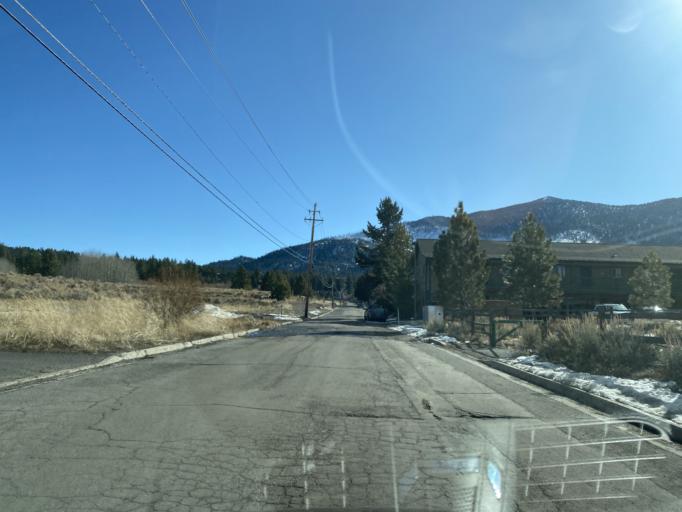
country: US
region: Nevada
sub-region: Douglas County
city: Kingsbury
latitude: 38.9729
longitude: -119.9412
